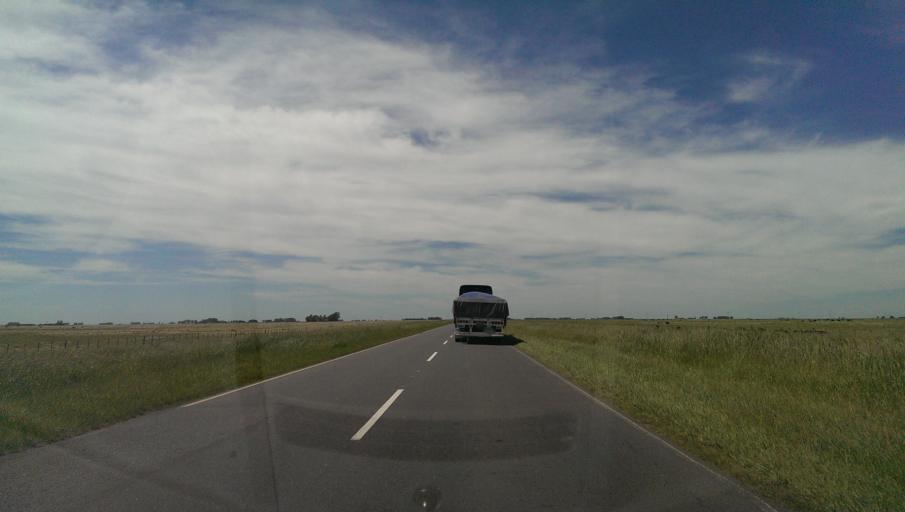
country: AR
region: Buenos Aires
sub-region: Partido de Laprida
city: Laprida
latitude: -37.2419
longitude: -60.7765
